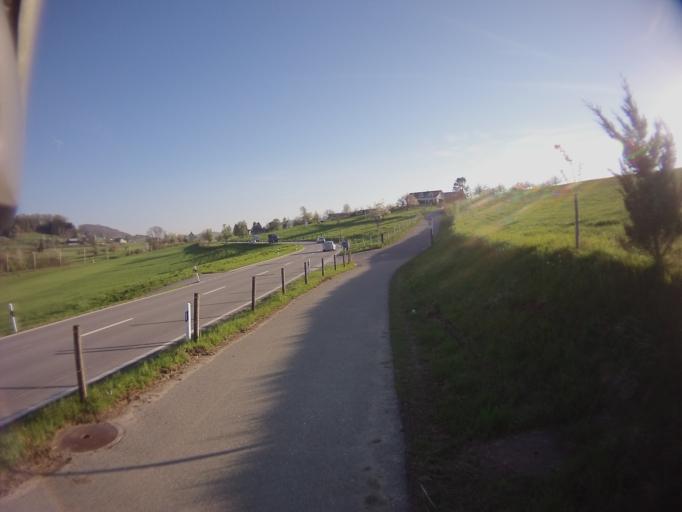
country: CH
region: Zurich
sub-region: Bezirk Affoltern
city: Bonstetten
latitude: 47.3122
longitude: 8.4581
